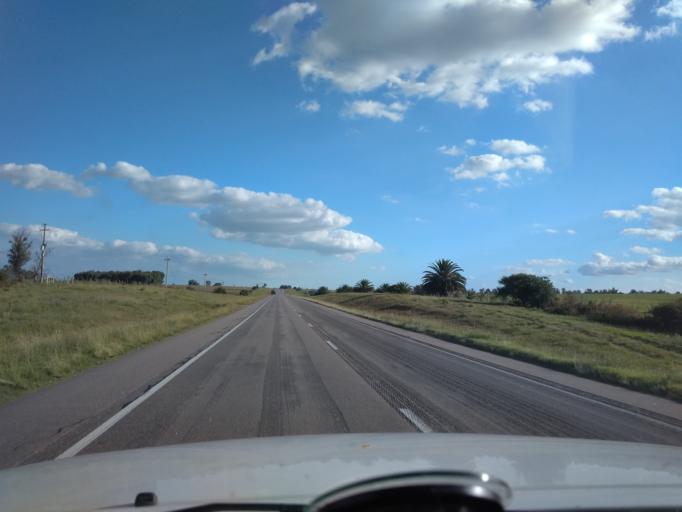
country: UY
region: Florida
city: Florida
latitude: -34.2172
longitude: -56.2077
